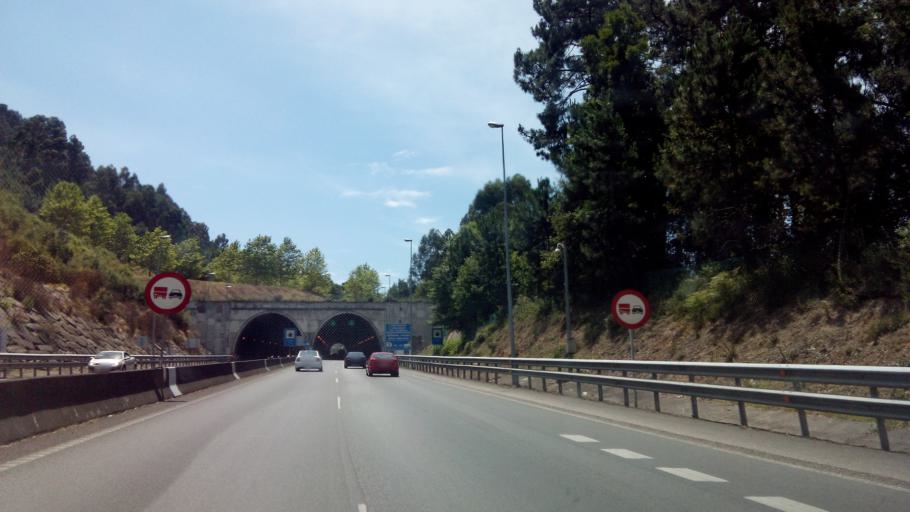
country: ES
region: Galicia
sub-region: Provincia de Pontevedra
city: Vigo
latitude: 42.2551
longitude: -8.6765
